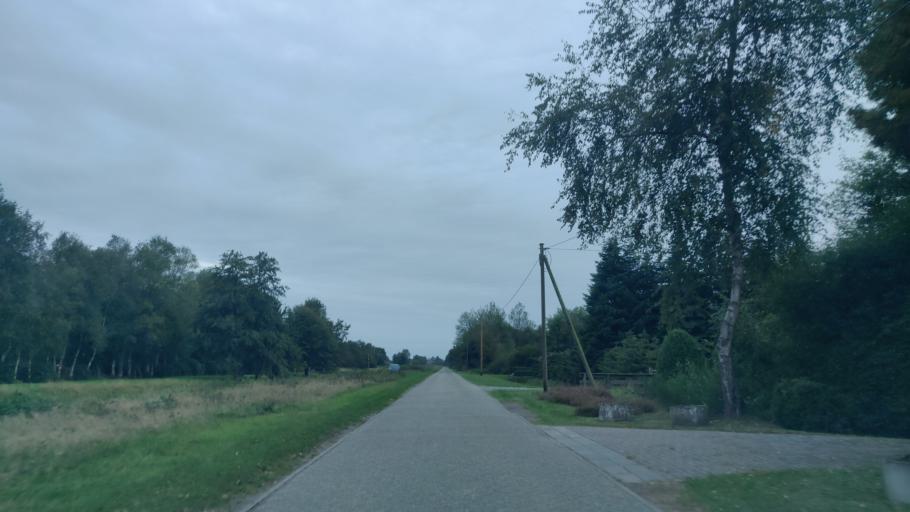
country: DE
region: Lower Saxony
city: Aurich
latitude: 53.4905
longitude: 7.4147
